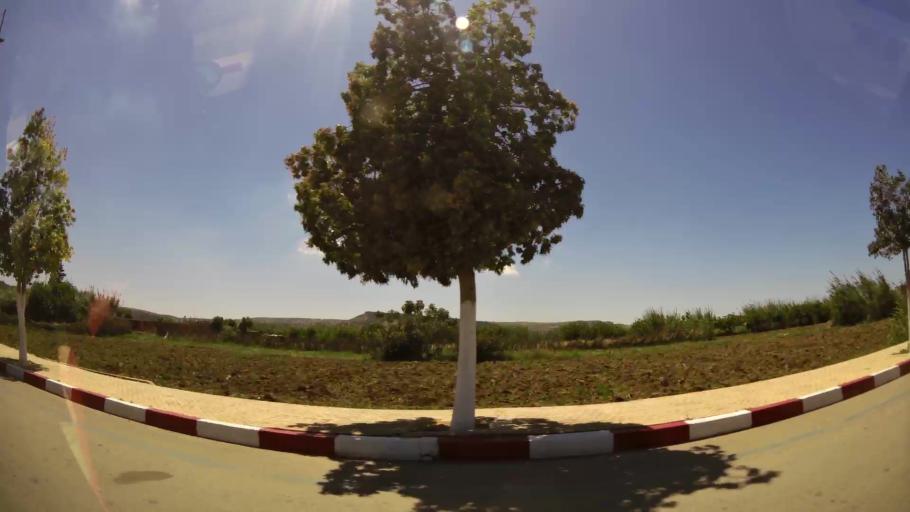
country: MA
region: Oriental
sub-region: Berkane-Taourirt
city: Madagh
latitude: 35.0705
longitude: -2.2176
